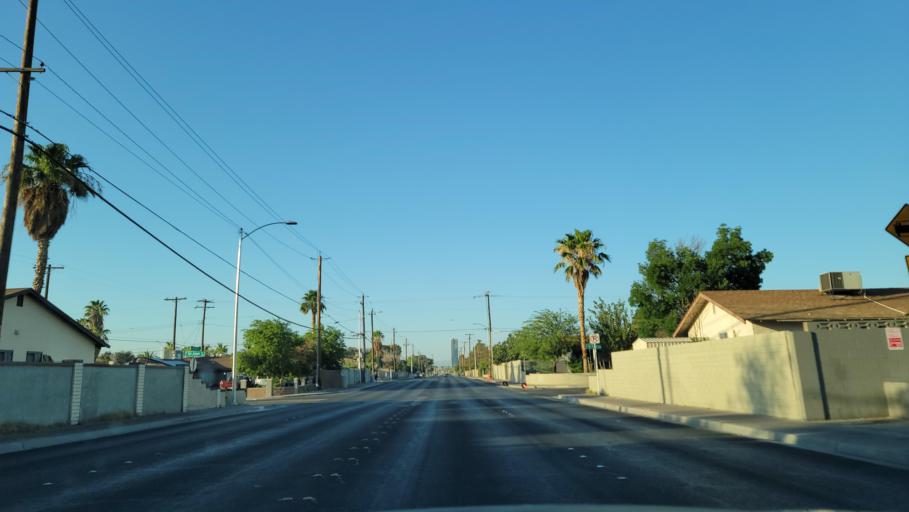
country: US
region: Nevada
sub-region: Clark County
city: Spring Valley
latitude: 36.1419
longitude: -115.1997
